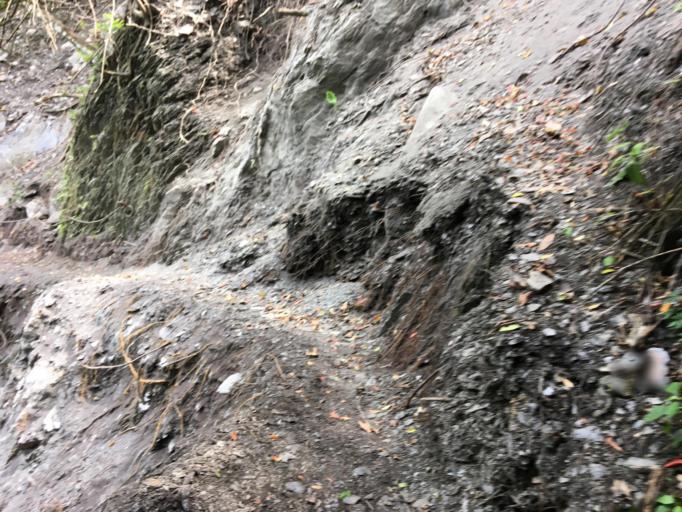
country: TW
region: Taiwan
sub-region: Yilan
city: Yilan
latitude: 24.4251
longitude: 121.7019
